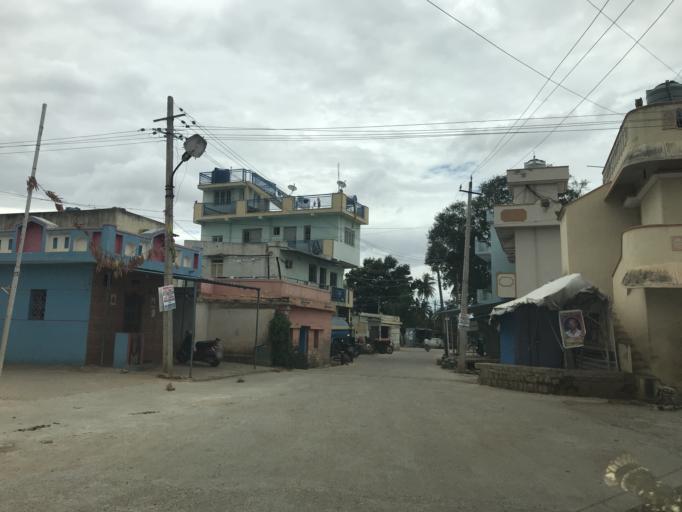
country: IN
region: Karnataka
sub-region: Bangalore Rural
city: Devanhalli
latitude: 13.2148
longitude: 77.6670
